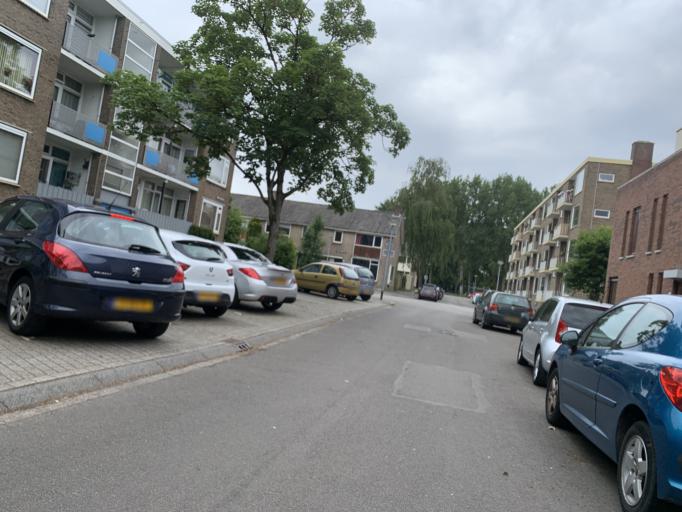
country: NL
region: Groningen
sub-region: Gemeente Groningen
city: Groningen
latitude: 53.1939
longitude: 6.5656
